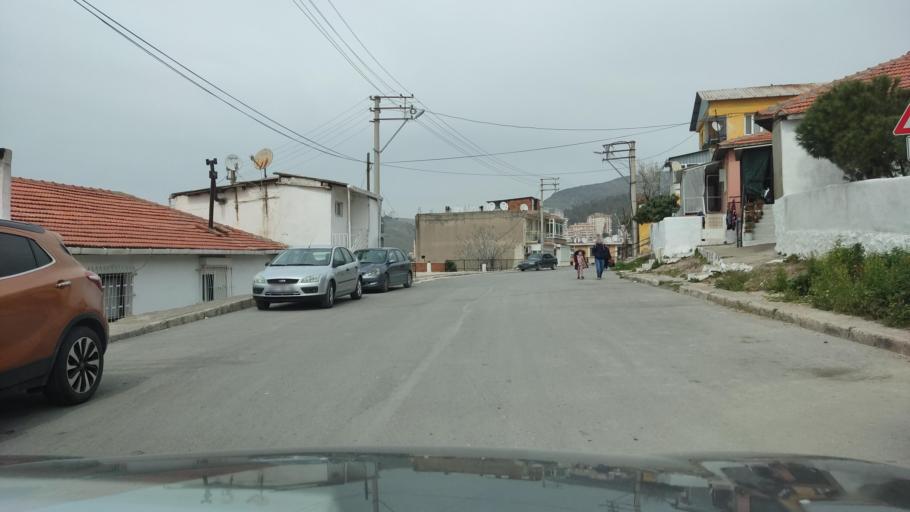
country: TR
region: Izmir
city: Karsiyaka
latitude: 38.4967
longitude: 27.0710
